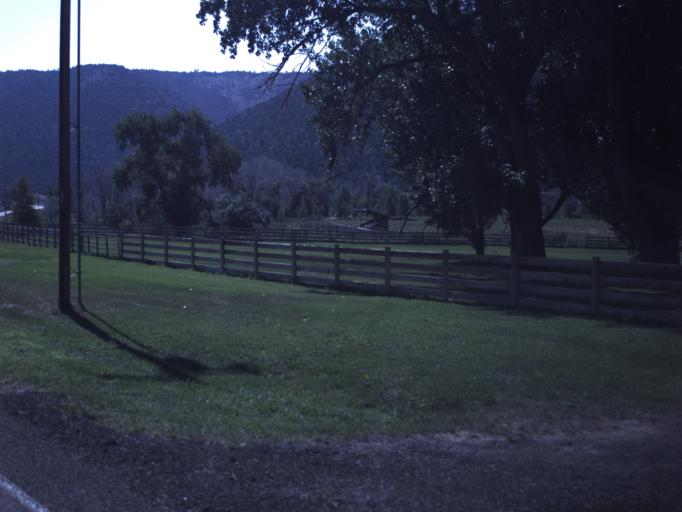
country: US
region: Utah
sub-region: Duchesne County
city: Duchesne
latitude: 40.3019
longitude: -110.6081
